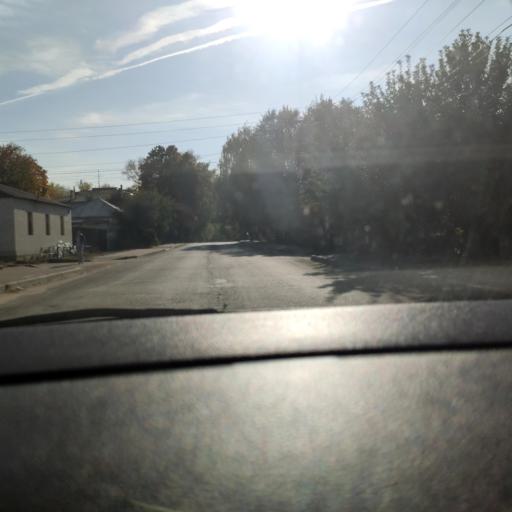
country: RU
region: Voronezj
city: Voronezh
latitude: 51.6799
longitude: 39.1394
